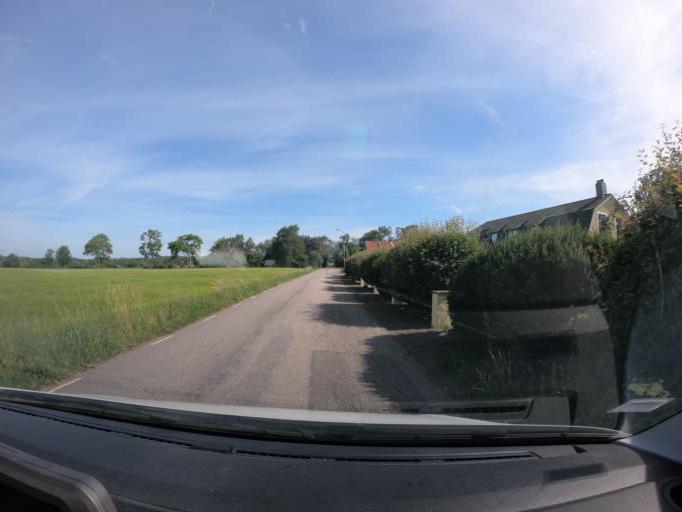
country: SE
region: Skane
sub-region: Bastads Kommun
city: Forslov
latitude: 56.3751
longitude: 12.7867
